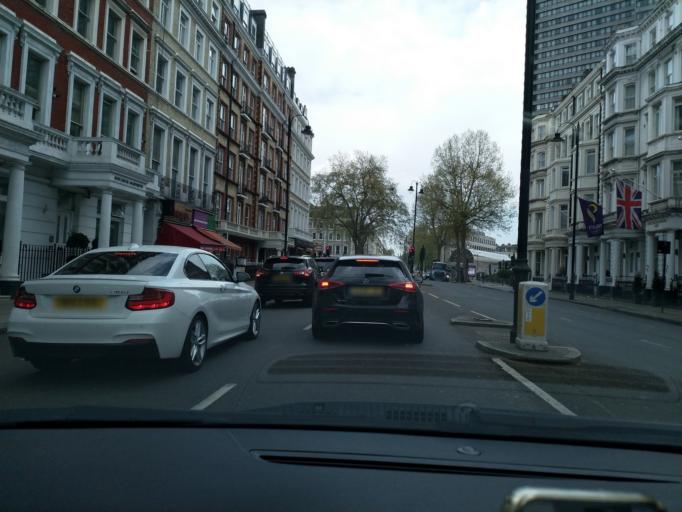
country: GB
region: England
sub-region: Greater London
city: Kensington
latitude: 51.4947
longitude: -0.1871
